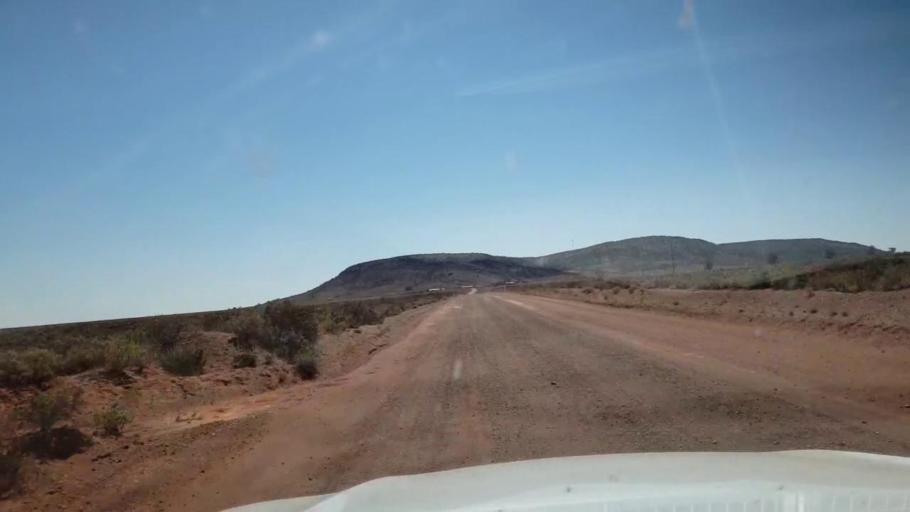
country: AU
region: South Australia
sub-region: Whyalla
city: Whyalla
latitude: -32.6990
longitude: 137.1333
